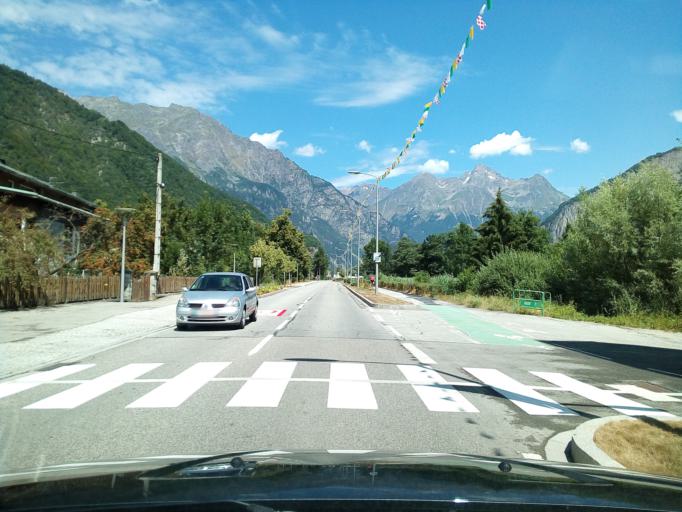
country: FR
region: Rhone-Alpes
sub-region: Departement de l'Isere
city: Huez
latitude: 45.0598
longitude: 6.0275
